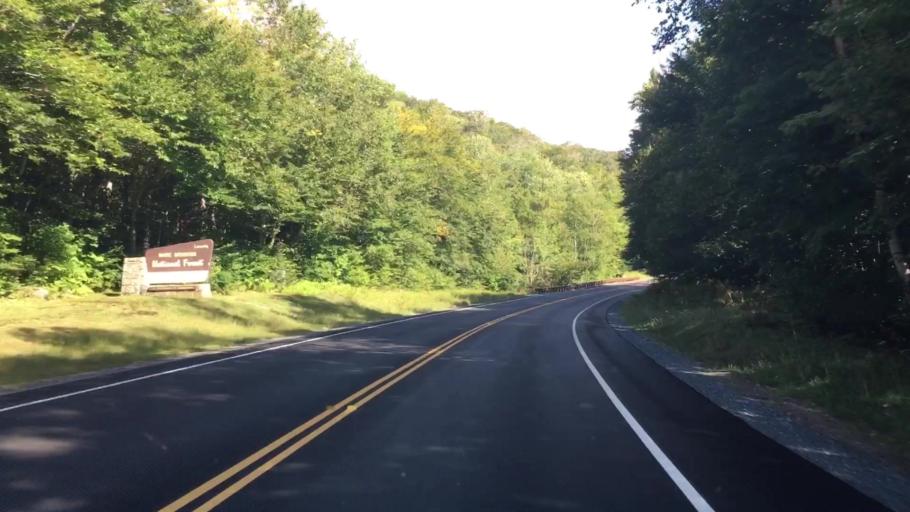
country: US
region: New Hampshire
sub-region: Grafton County
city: Woodstock
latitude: 44.0268
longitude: -71.7560
